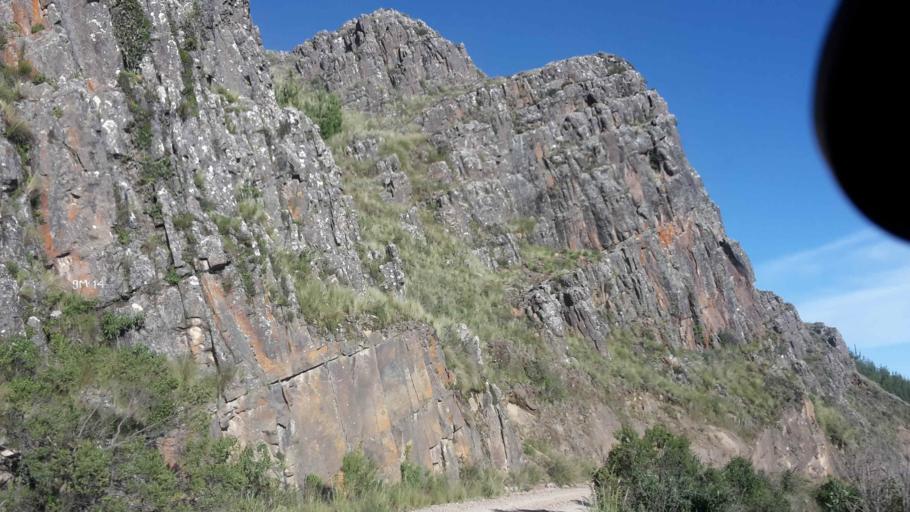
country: BO
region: Cochabamba
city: Arani
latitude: -17.7190
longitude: -65.6515
